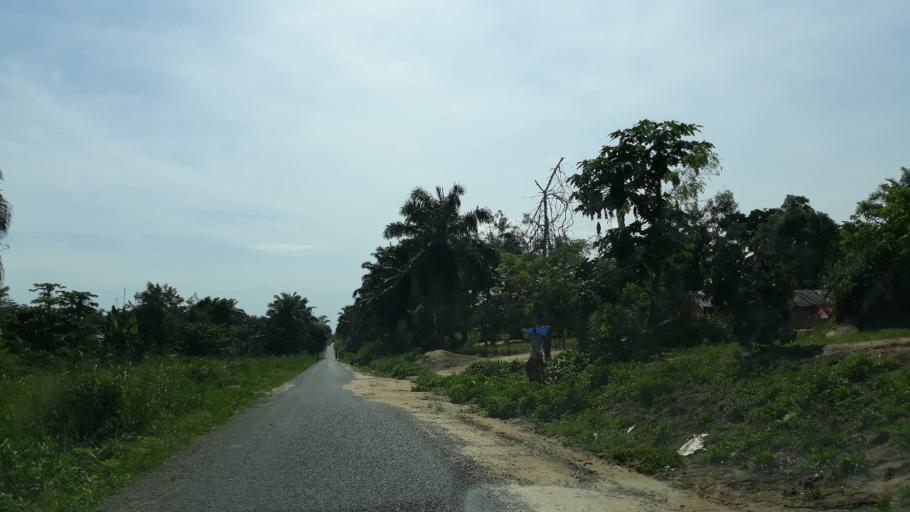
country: CD
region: Maniema
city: Kindu
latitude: -2.9092
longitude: 26.0261
